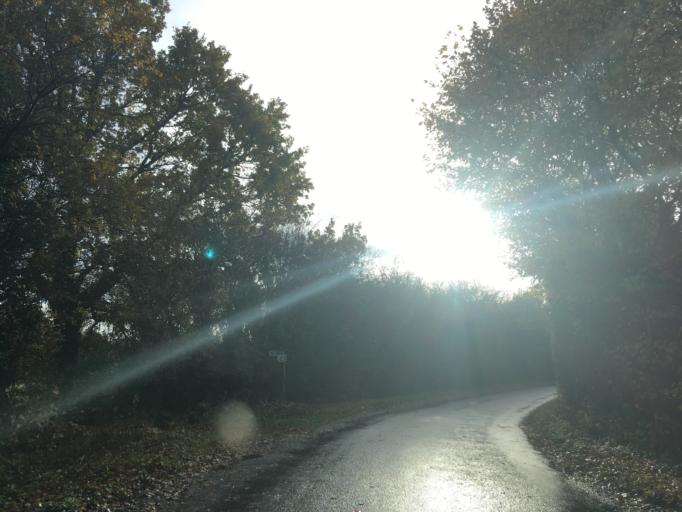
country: GB
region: England
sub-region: South Gloucestershire
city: Winterbourne
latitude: 51.5133
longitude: -2.4791
